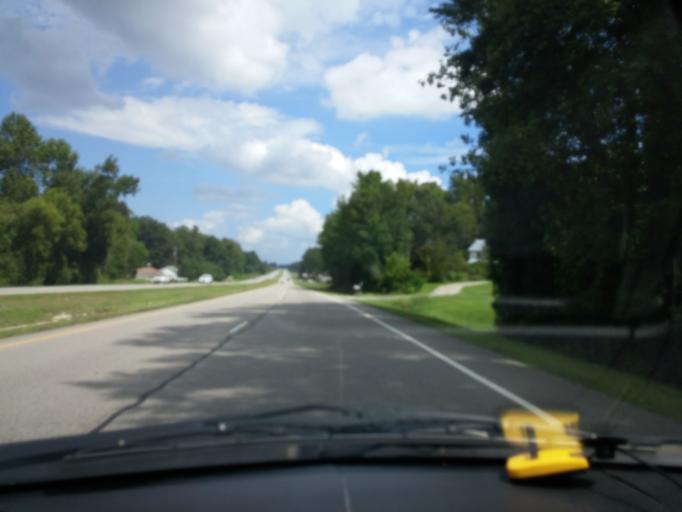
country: US
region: North Carolina
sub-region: Pitt County
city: Grifton
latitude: 35.3281
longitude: -77.4920
